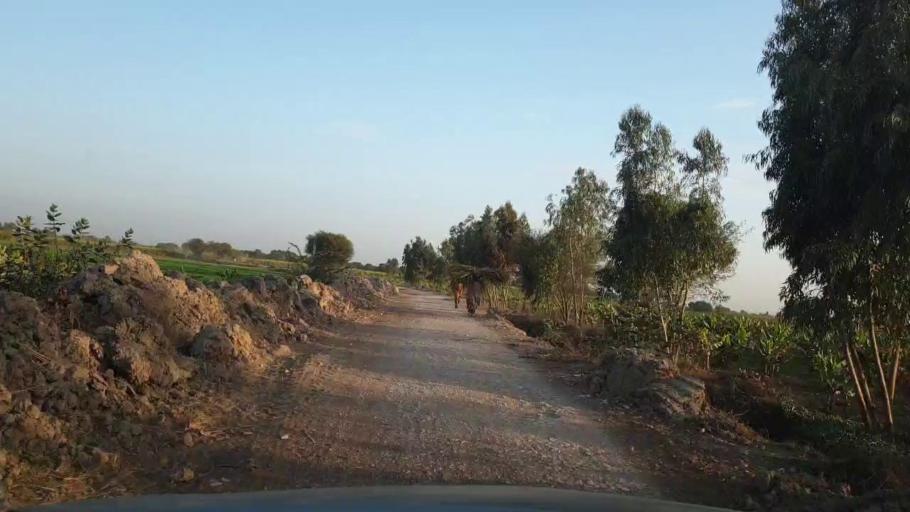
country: PK
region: Sindh
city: Matiari
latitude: 25.6157
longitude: 68.5305
